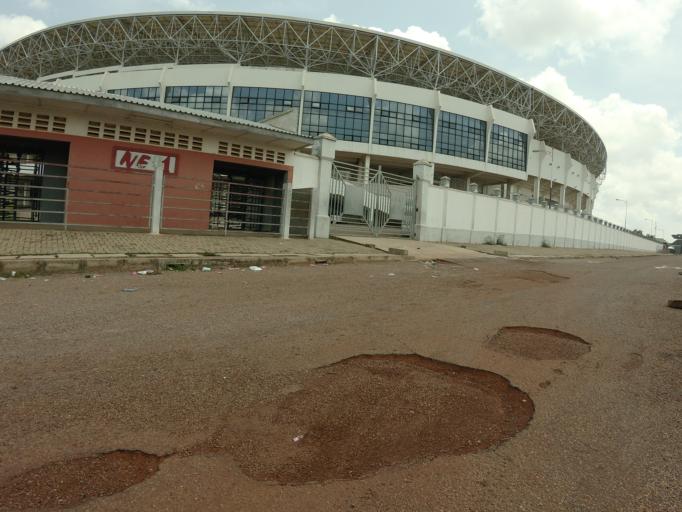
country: GH
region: Northern
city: Tamale
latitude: 9.4109
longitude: -0.8603
